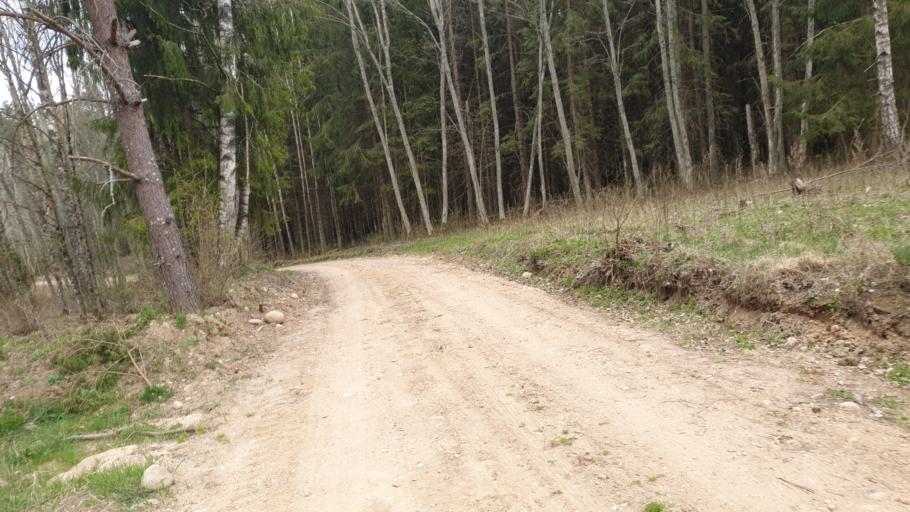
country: LT
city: Aukstadvaris
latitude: 54.5112
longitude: 24.6387
